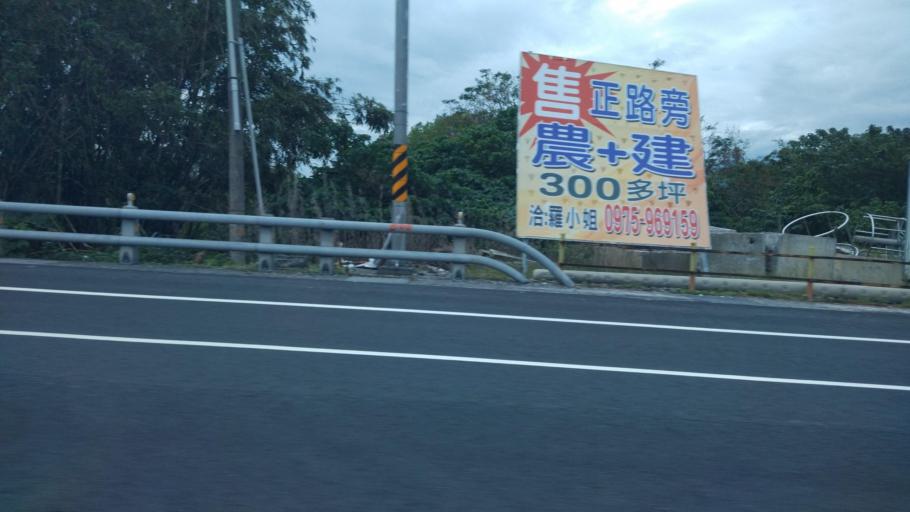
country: TW
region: Taiwan
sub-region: Hualien
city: Hualian
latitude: 24.0075
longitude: 121.6101
